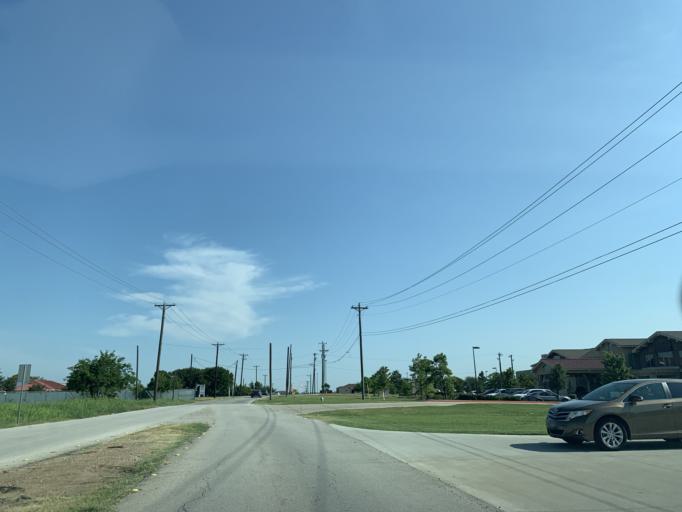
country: US
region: Texas
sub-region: Tarrant County
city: Blue Mound
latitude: 32.8968
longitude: -97.3069
